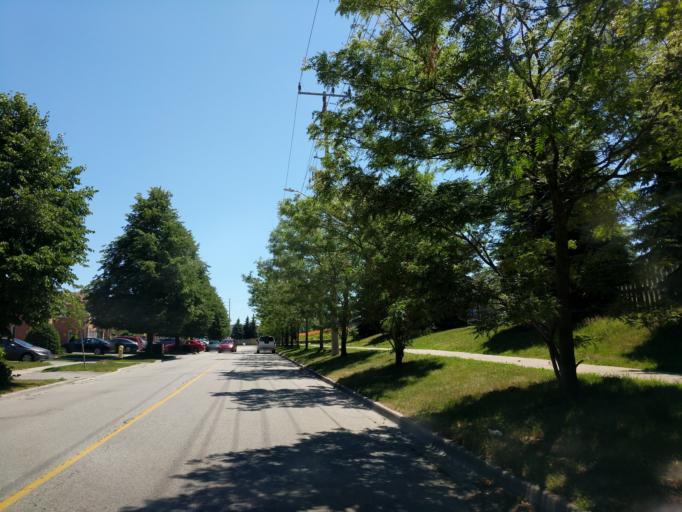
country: CA
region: Ontario
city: Ajax
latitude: 43.8488
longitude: -79.0697
